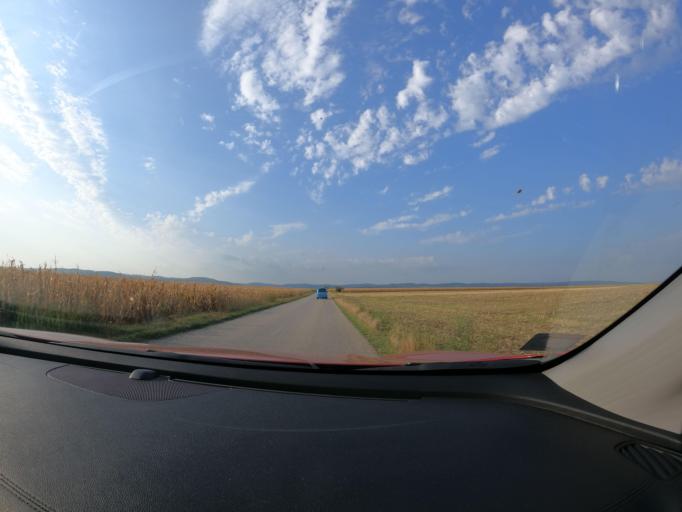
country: RS
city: Vrdnik
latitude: 45.0819
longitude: 19.8076
